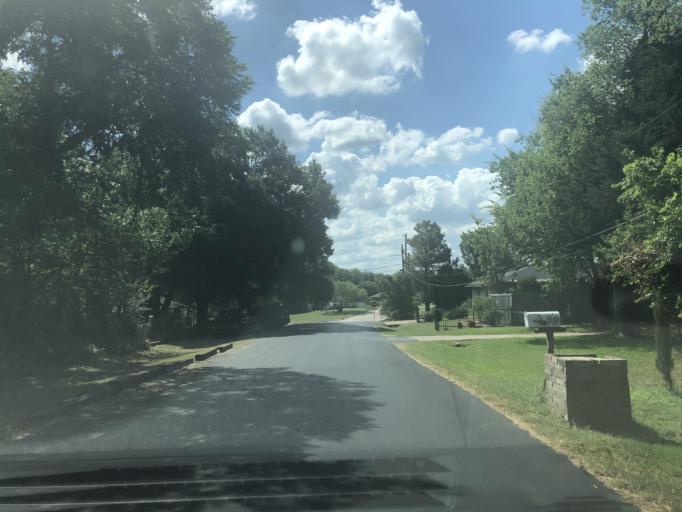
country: US
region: Texas
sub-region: Dallas County
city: Grand Prairie
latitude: 32.7381
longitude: -96.9996
